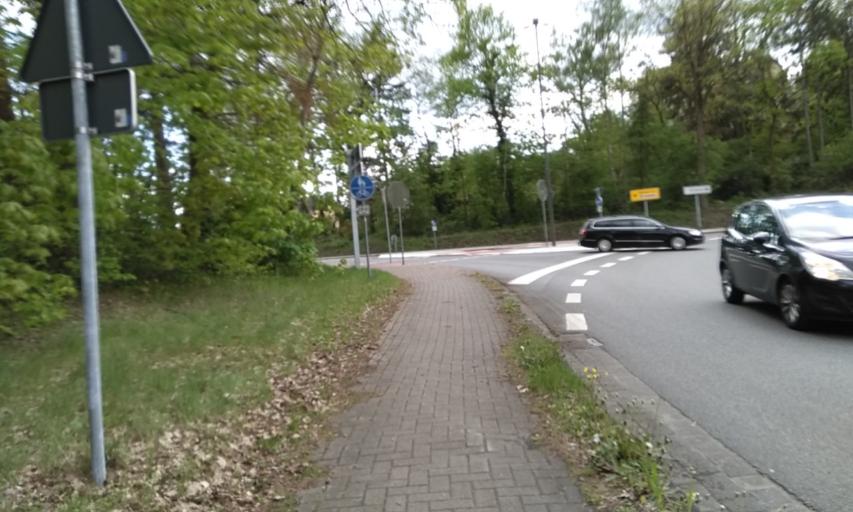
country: DE
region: Lower Saxony
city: Buxtehude
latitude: 53.4644
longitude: 9.6808
